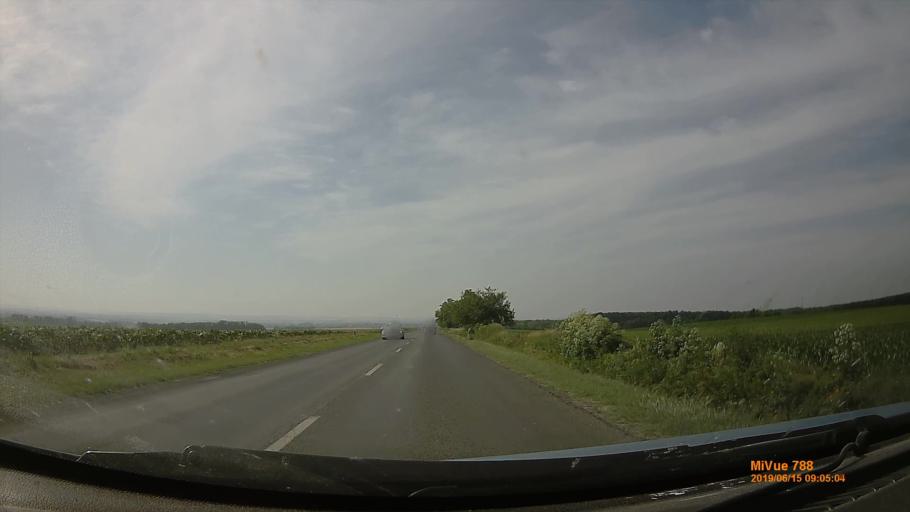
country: HU
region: Tolna
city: Iregszemcse
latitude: 46.7287
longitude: 18.1684
